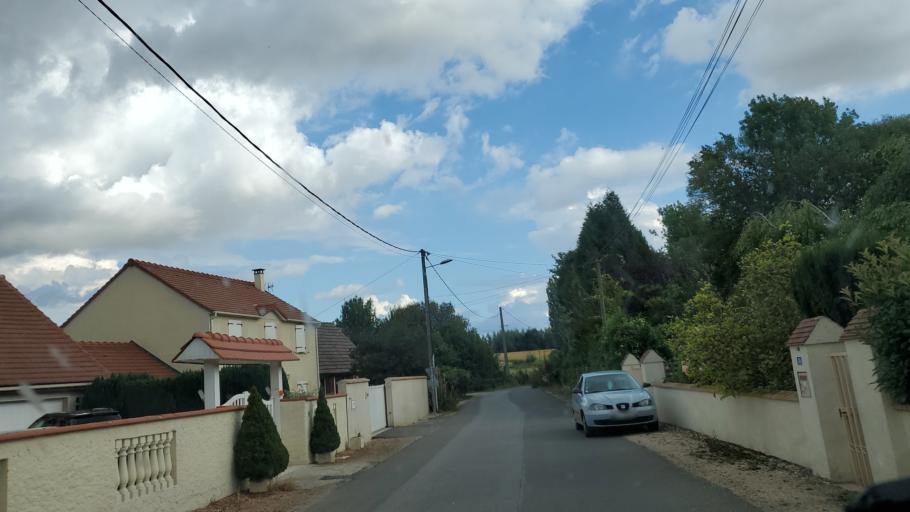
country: FR
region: Ile-de-France
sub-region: Departement de Seine-et-Marne
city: Chailly-en-Brie
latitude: 48.7753
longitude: 3.1647
